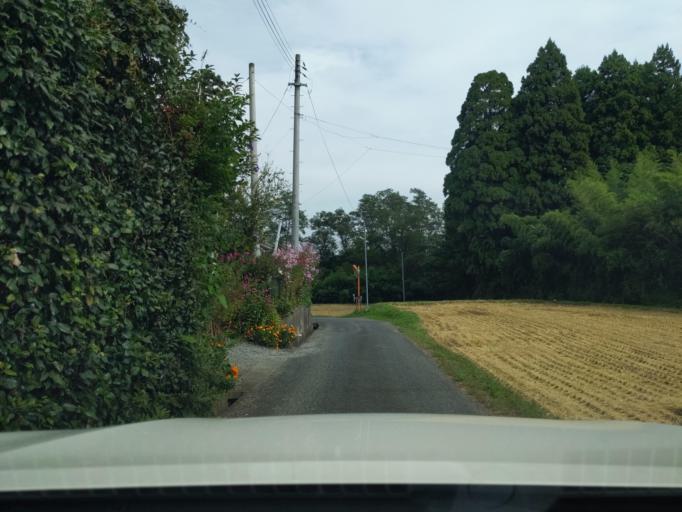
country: JP
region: Fukushima
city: Koriyama
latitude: 37.4137
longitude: 140.3230
